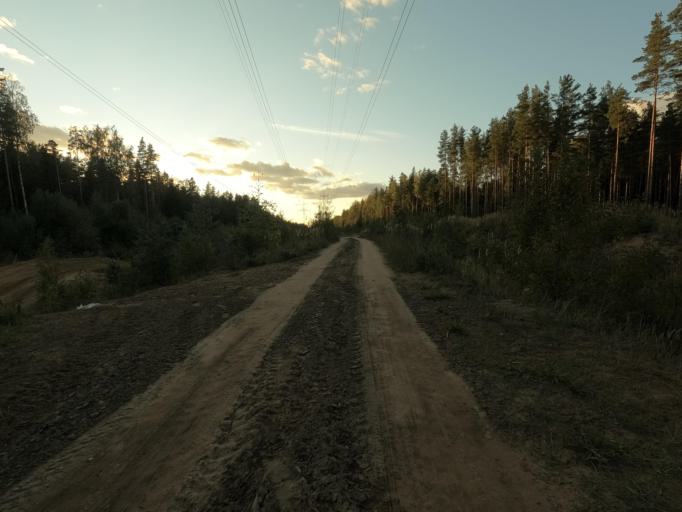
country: RU
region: Leningrad
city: Otradnoye
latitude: 59.8216
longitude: 30.8279
